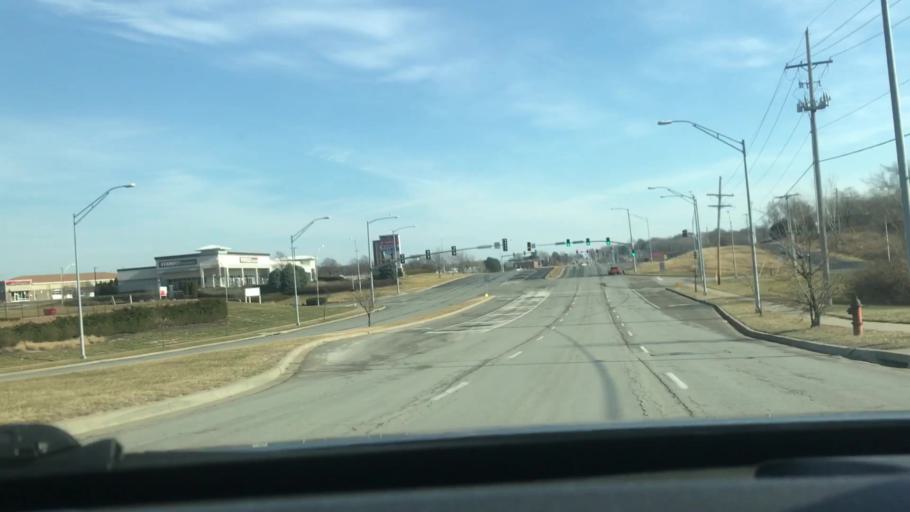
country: US
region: Missouri
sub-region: Clay County
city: Gladstone
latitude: 39.2463
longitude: -94.5963
